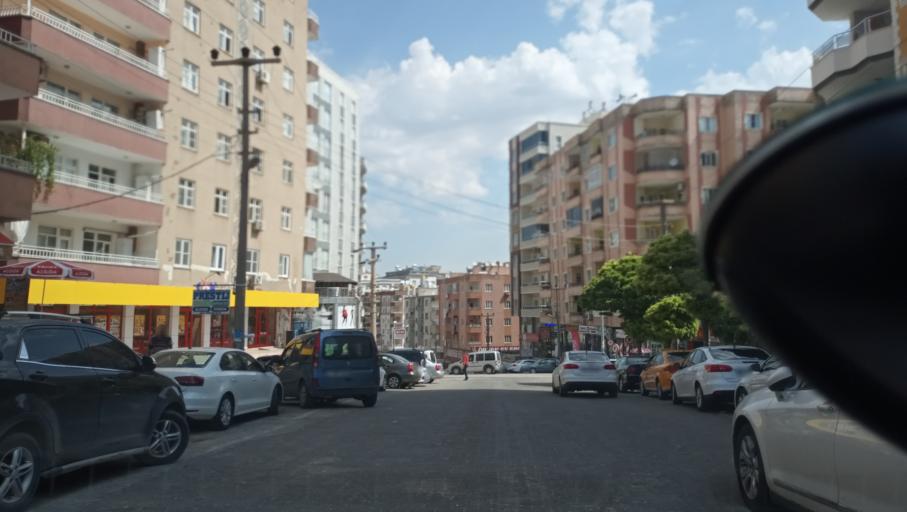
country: TR
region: Mardin
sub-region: Mardin Ilcesi
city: Mardin
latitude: 37.3262
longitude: 40.7174
